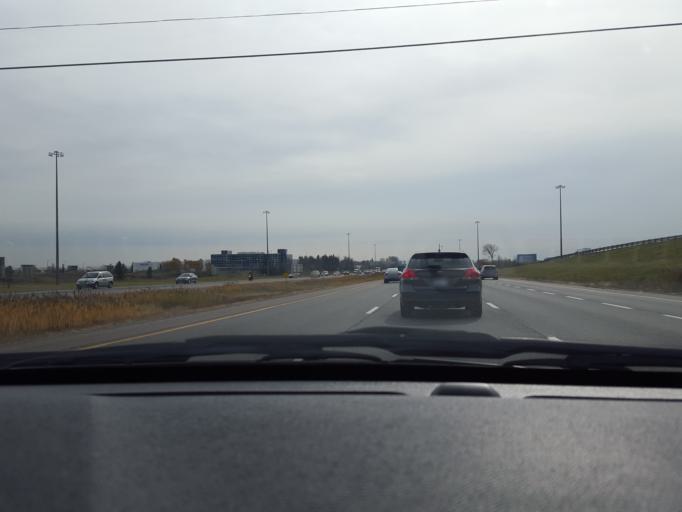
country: CA
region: Ontario
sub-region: York
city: Richmond Hill
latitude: 43.8831
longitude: -79.3800
